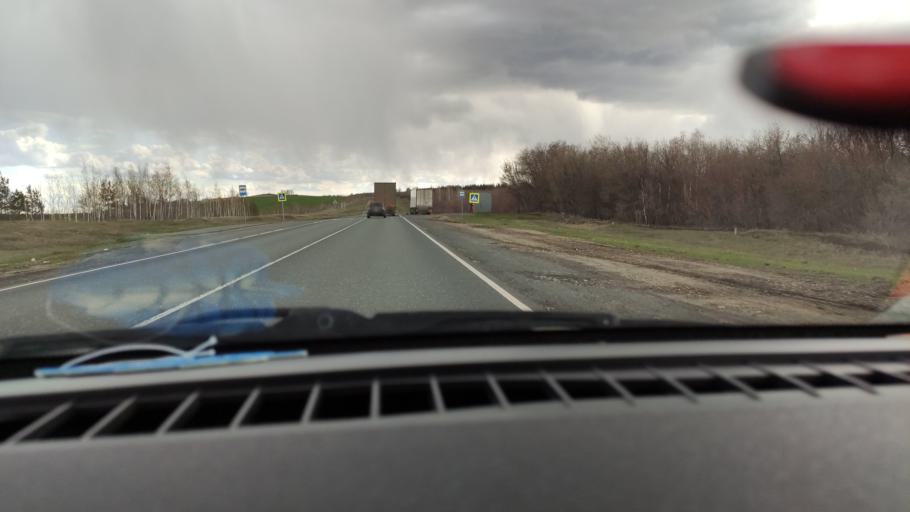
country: RU
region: Saratov
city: Balakovo
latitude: 52.1735
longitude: 47.8334
